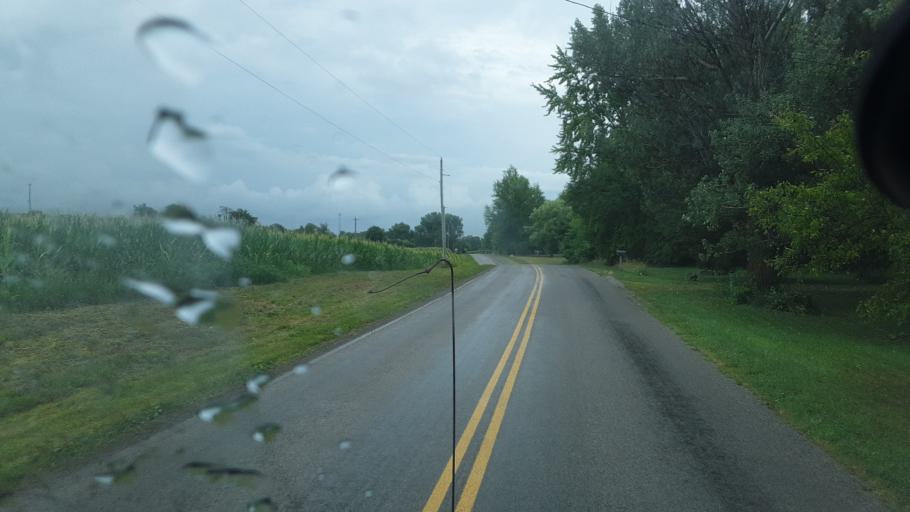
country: US
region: Indiana
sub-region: Steuben County
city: Hamilton
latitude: 41.6435
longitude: -84.7909
